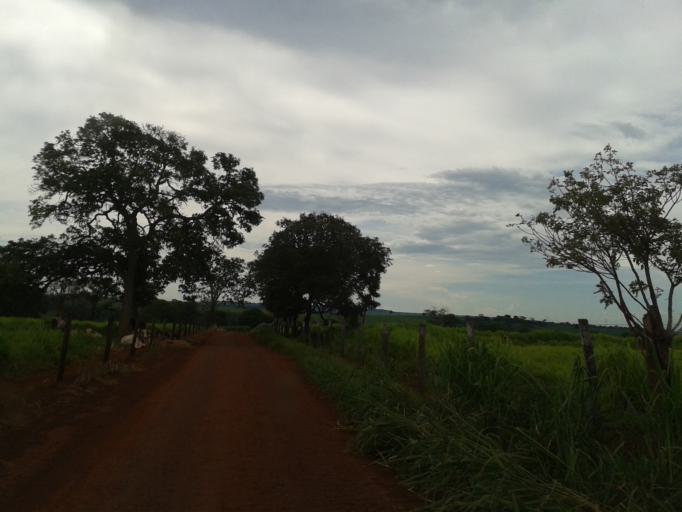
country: BR
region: Minas Gerais
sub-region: Centralina
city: Centralina
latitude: -18.6777
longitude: -49.3589
